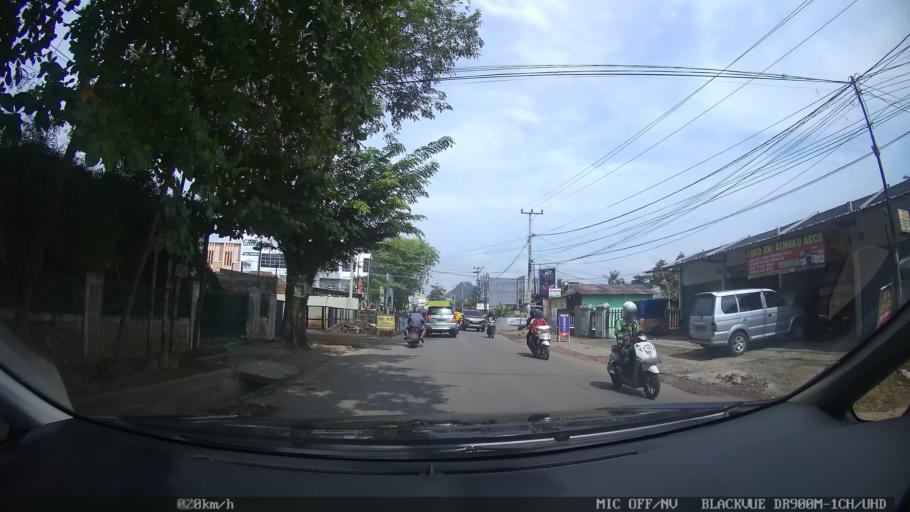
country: ID
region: Lampung
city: Kedaton
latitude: -5.3917
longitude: 105.2820
